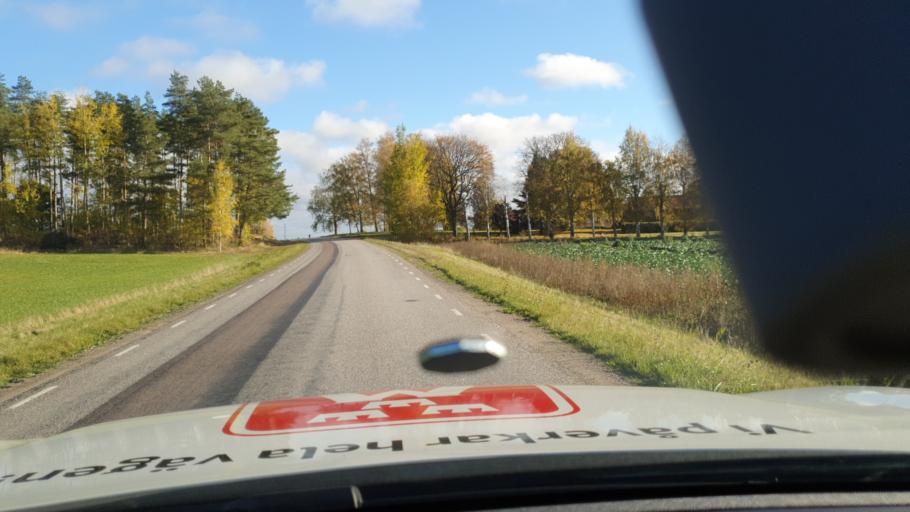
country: SE
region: OEstergoetland
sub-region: Motala Kommun
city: Borensberg
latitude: 58.5211
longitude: 15.2213
